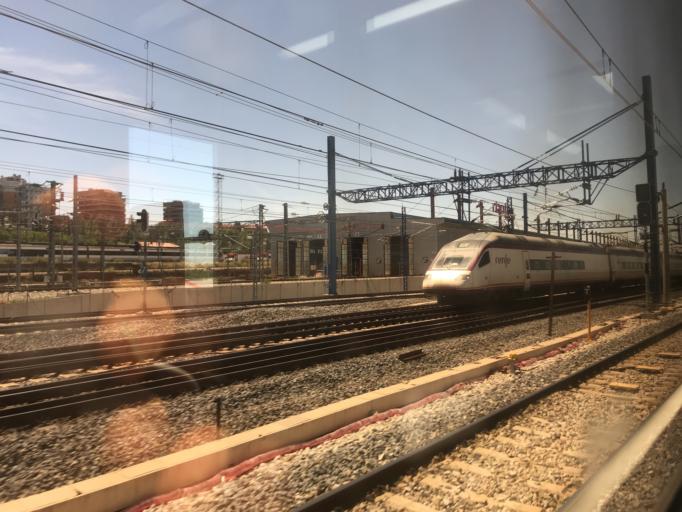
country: ES
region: Madrid
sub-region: Provincia de Madrid
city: Puente de Vallecas
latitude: 40.3871
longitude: -3.6759
